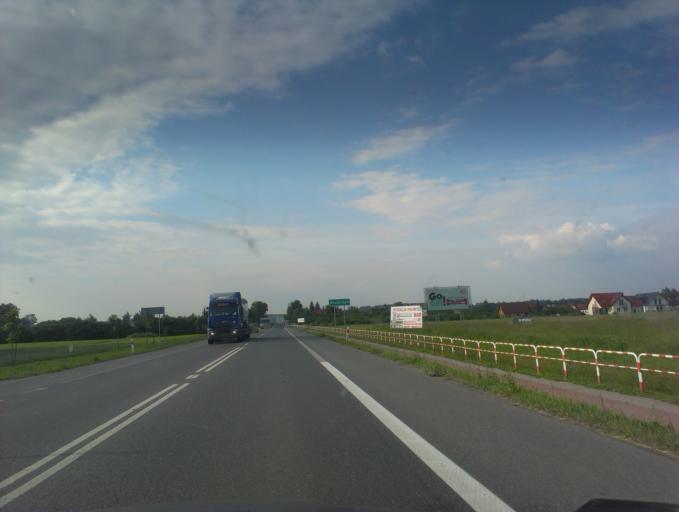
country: PL
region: Lower Silesian Voivodeship
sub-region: Powiat trzebnicki
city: Psary
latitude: 51.2405
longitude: 17.0441
